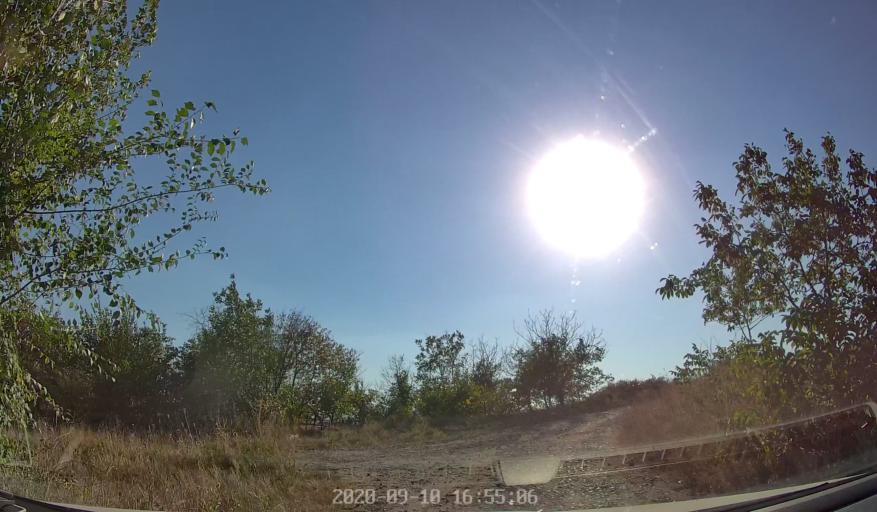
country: MD
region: Chisinau
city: Stauceni
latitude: 47.0538
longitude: 28.9204
